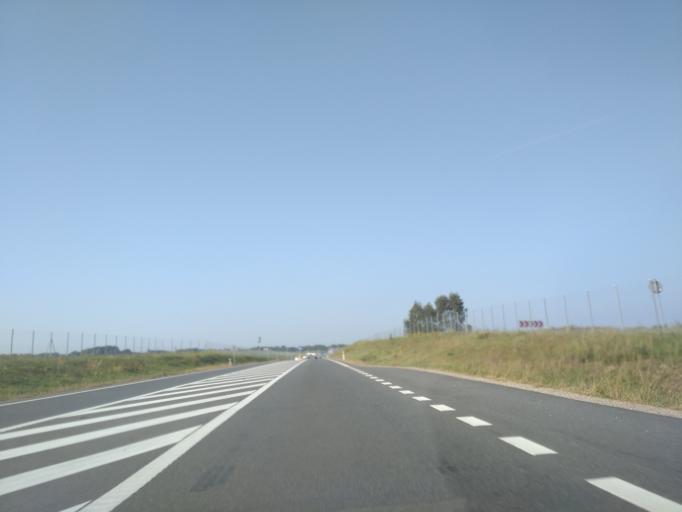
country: PL
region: Subcarpathian Voivodeship
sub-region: Powiat rzeszowski
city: Sokolow Malopolski
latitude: 50.2136
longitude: 22.1221
